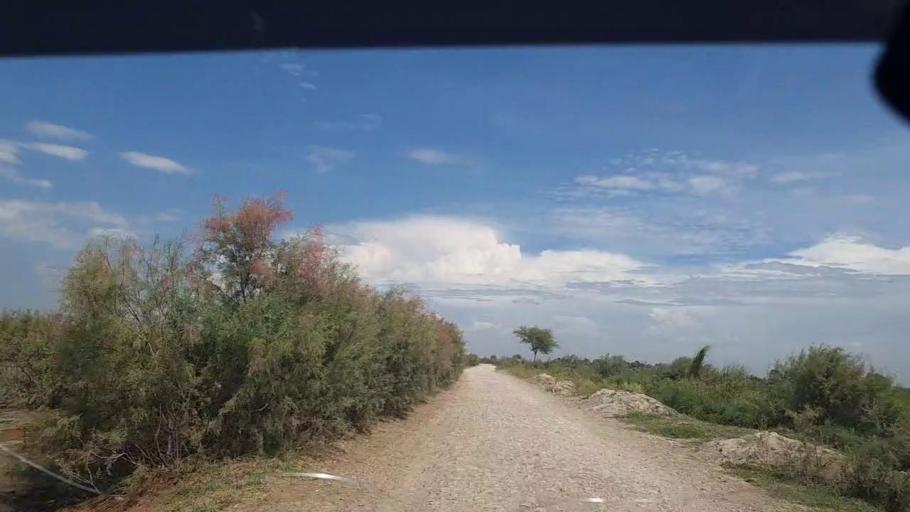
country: PK
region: Sindh
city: Ghauspur
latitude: 28.1477
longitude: 68.9738
